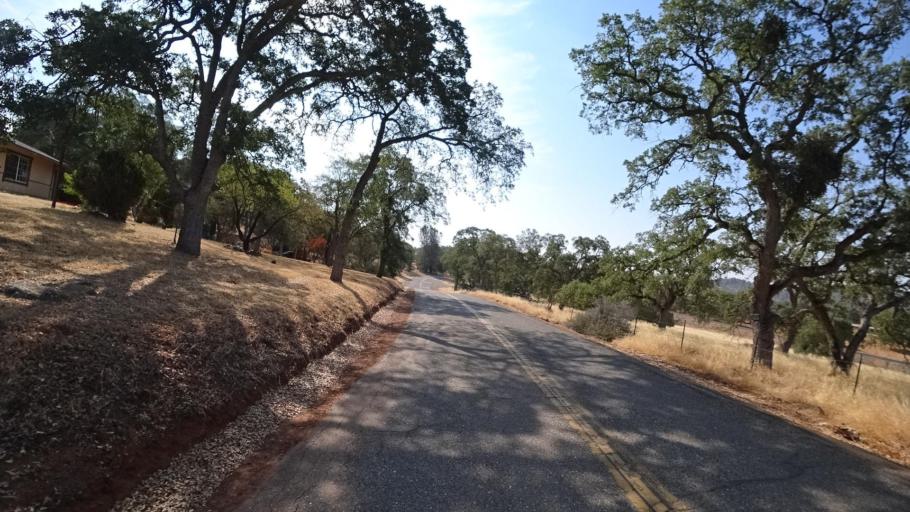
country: US
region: California
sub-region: Tuolumne County
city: Tuolumne City
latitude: 37.7017
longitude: -120.2904
